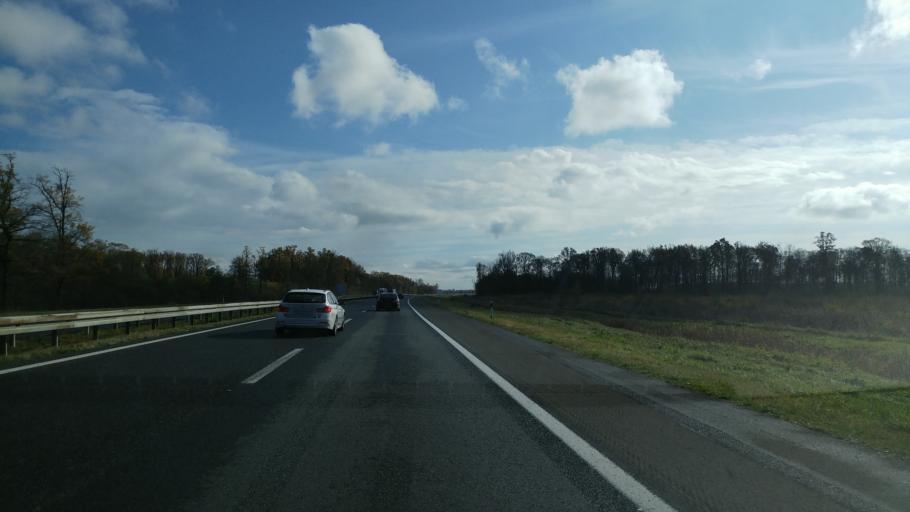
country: HR
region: Zagrebacka
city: Lupoglav
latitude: 45.7417
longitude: 16.3258
